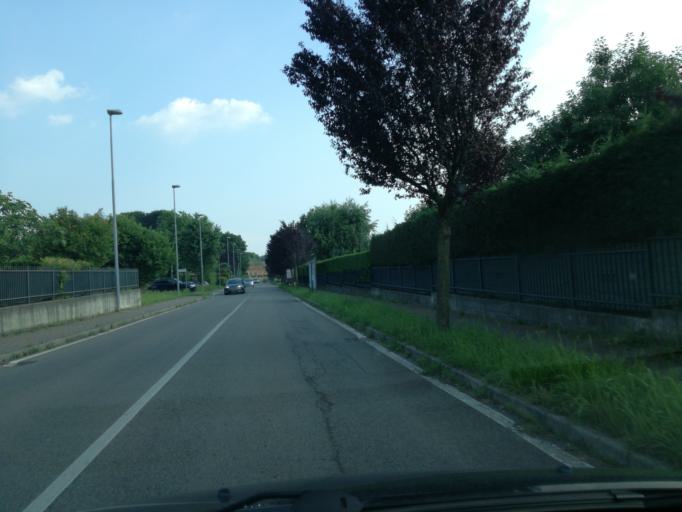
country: IT
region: Lombardy
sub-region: Provincia di Lecco
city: Paderno d'Adda
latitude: 45.6827
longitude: 9.4408
